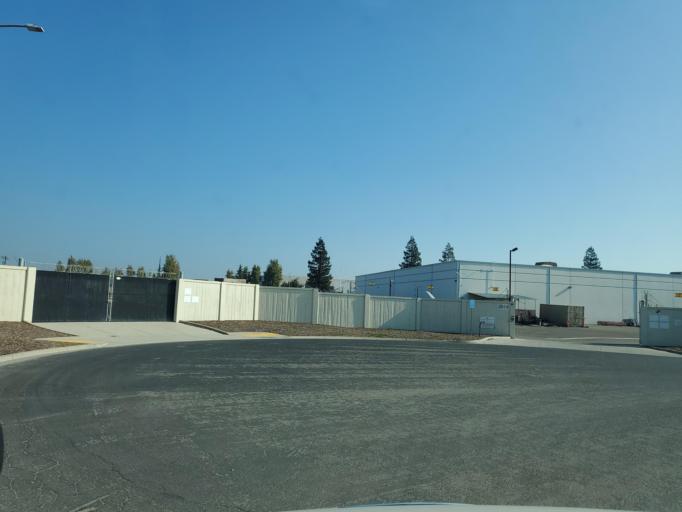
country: US
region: California
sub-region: San Joaquin County
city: Kennedy
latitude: 37.9162
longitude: -121.2625
